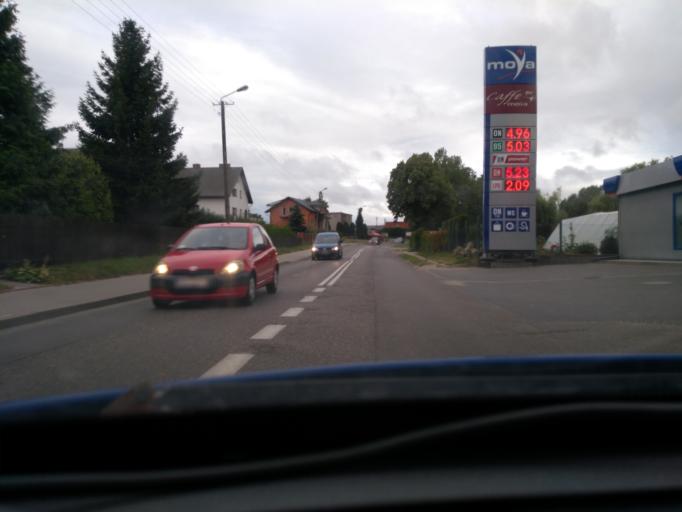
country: PL
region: Pomeranian Voivodeship
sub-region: Powiat kartuski
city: Banino
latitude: 54.3691
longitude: 18.3927
